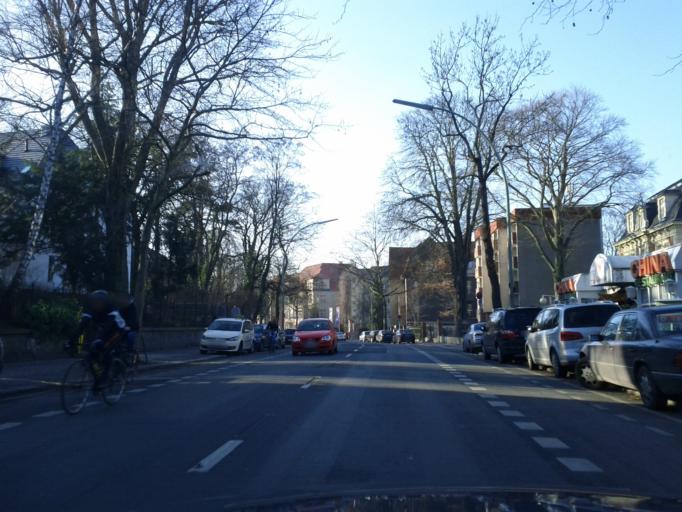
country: DE
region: Berlin
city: Friedenau
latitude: 52.4598
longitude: 13.3125
